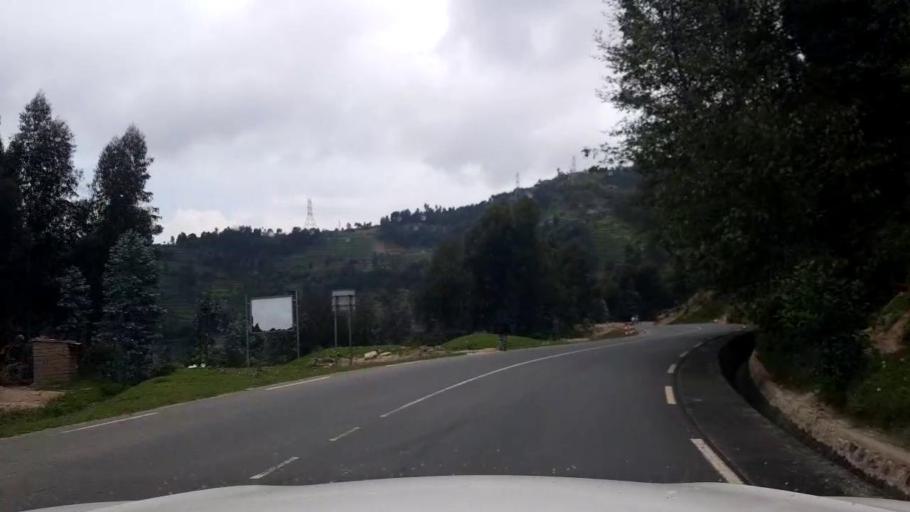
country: RW
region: Northern Province
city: Musanze
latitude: -1.6589
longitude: 29.5129
